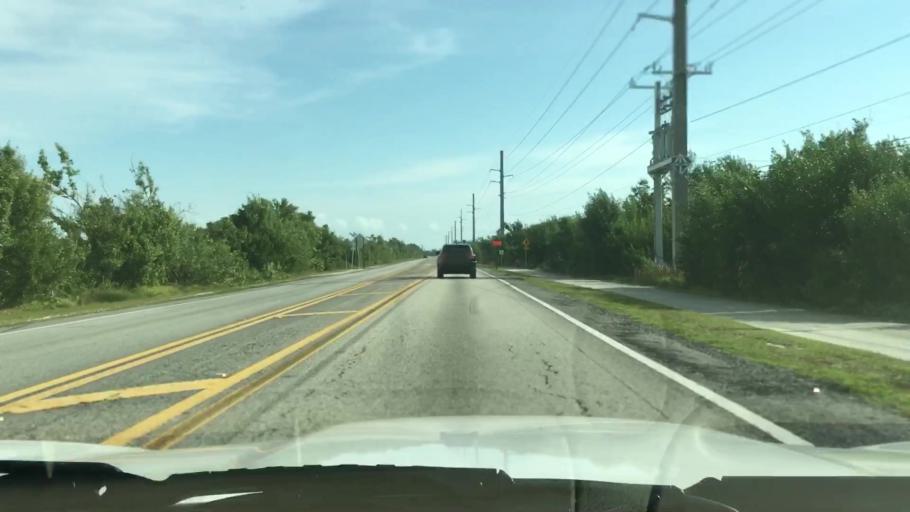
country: US
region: Florida
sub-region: Monroe County
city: Cudjoe Key
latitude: 24.6637
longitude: -81.5096
